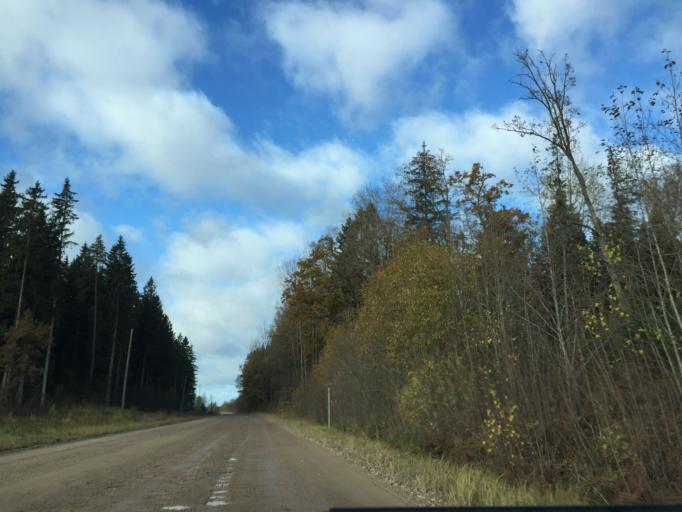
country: LV
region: Engure
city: Smarde
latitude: 56.9633
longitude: 23.2489
